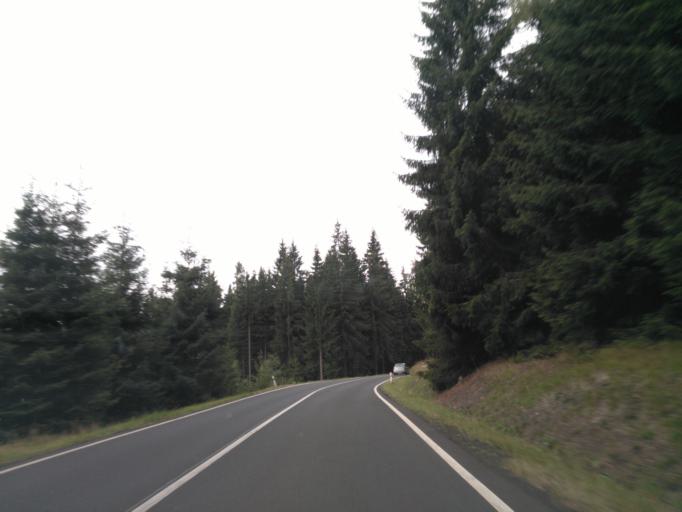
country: CZ
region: Karlovarsky
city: Merklin
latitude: 50.3798
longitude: 12.8798
